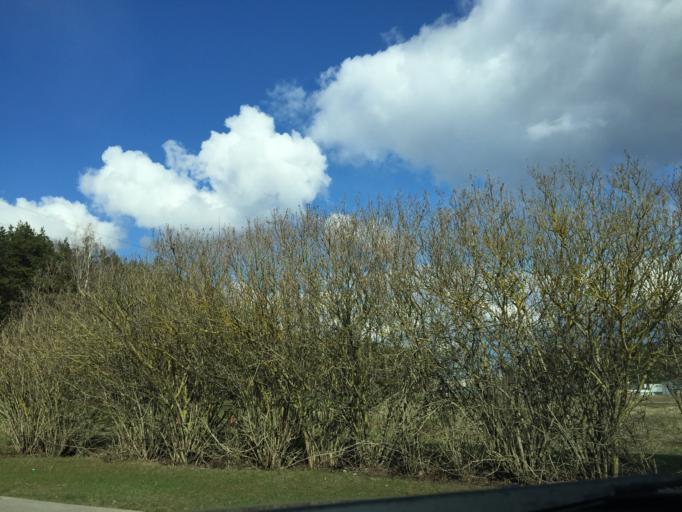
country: LV
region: Kekava
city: Kekava
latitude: 56.8215
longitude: 24.2164
